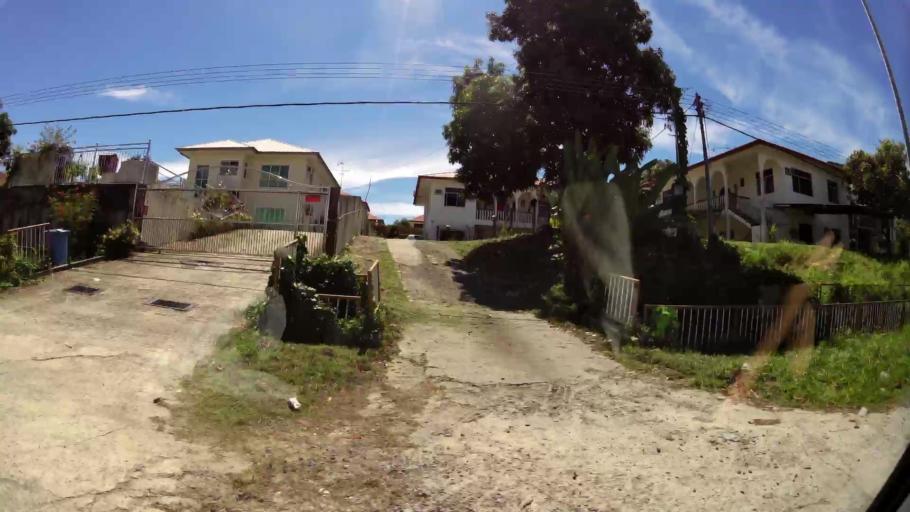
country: BN
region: Brunei and Muara
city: Bandar Seri Begawan
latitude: 5.0199
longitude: 115.0577
